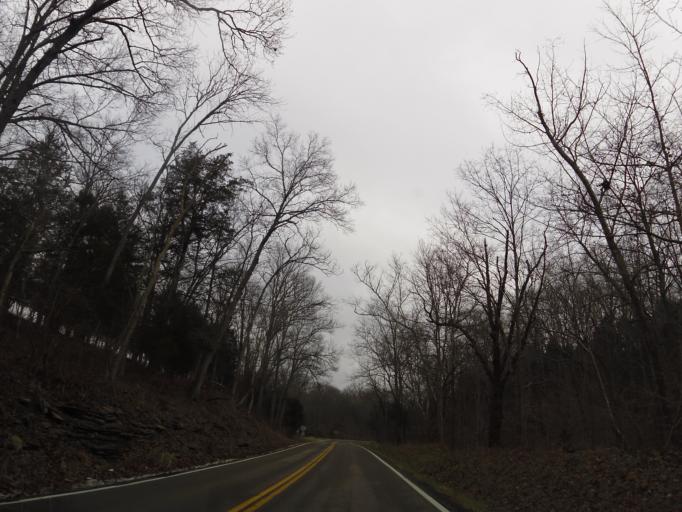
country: US
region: Kentucky
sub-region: Trimble County
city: Providence
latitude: 38.5471
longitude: -85.2648
